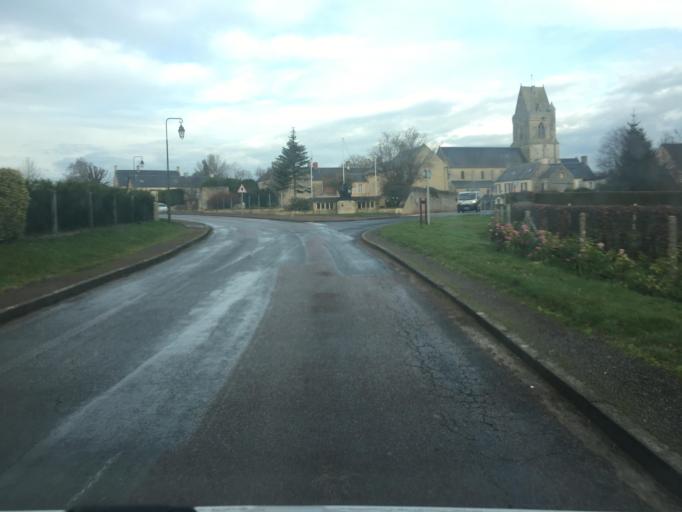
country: FR
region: Lower Normandy
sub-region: Departement du Calvados
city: Ver-sur-Mer
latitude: 49.3152
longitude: -0.5498
